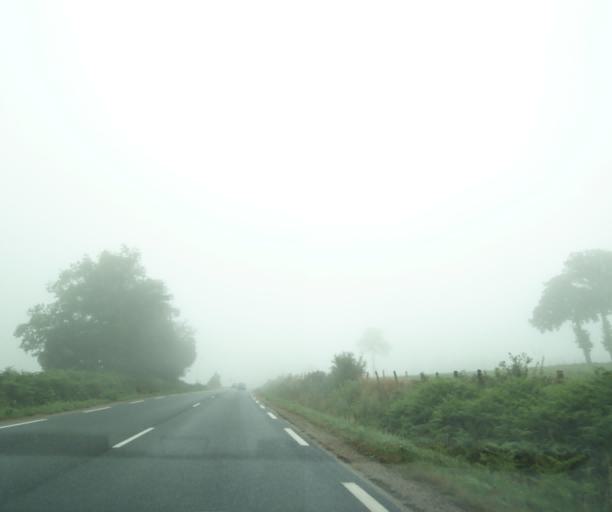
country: FR
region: Midi-Pyrenees
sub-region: Departement de l'Aveyron
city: Baraqueville
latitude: 44.2612
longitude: 2.4171
